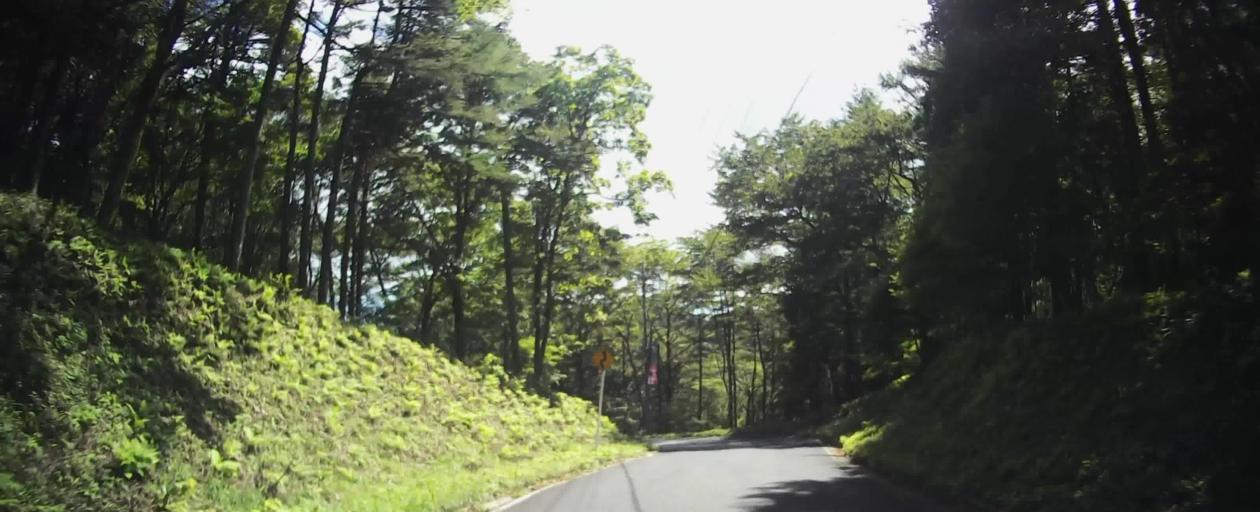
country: JP
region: Gunma
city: Nakanojomachi
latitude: 36.4747
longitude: 138.8728
